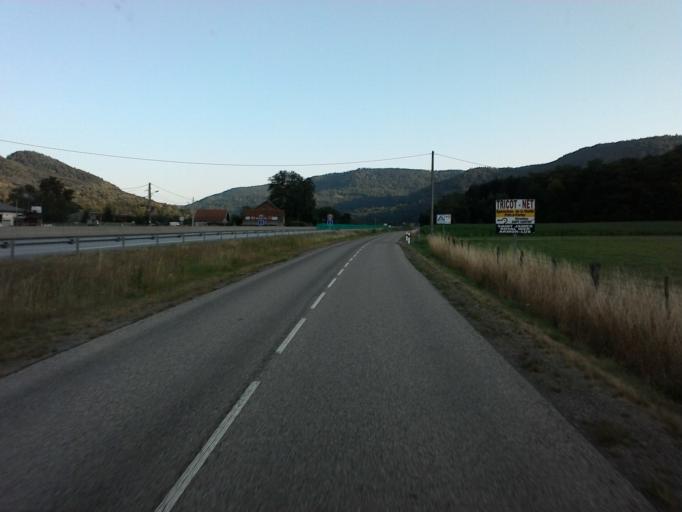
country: FR
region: Lorraine
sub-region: Departement des Vosges
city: Vecoux
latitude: 47.9655
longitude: 6.6294
